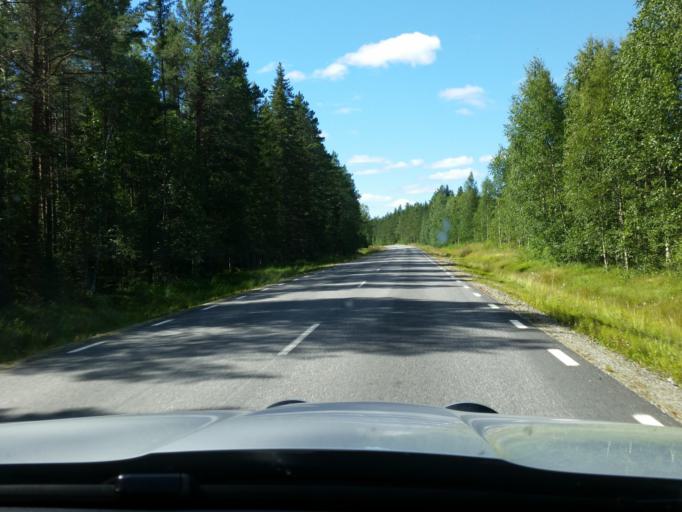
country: SE
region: Norrbotten
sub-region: Pitea Kommun
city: Roknas
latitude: 65.1896
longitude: 21.0741
